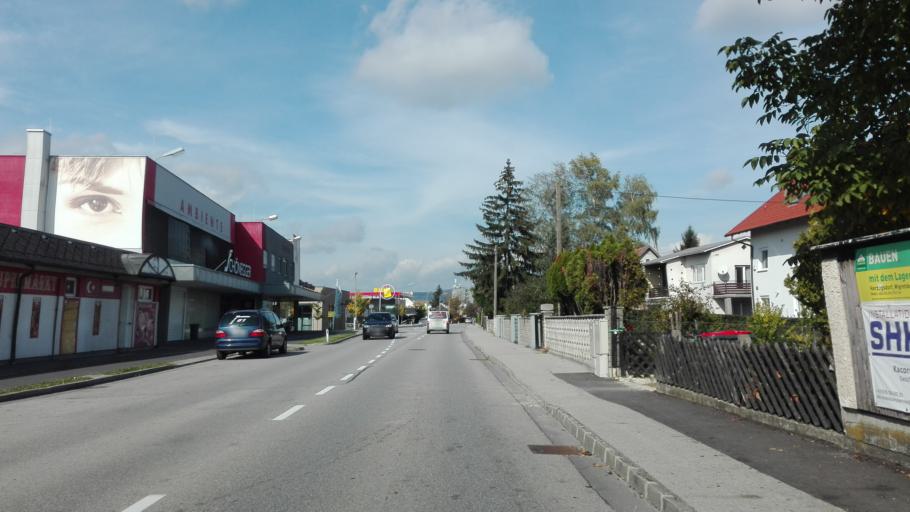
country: AT
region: Upper Austria
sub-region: Politischer Bezirk Linz-Land
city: Traun
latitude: 48.2400
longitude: 14.2612
